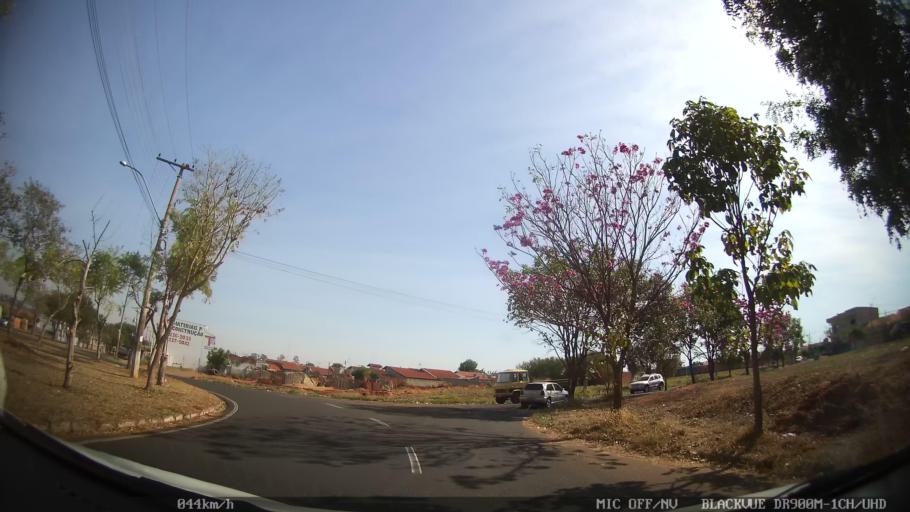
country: BR
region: Sao Paulo
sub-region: Sao Jose Do Rio Preto
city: Sao Jose do Rio Preto
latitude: -20.7903
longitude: -49.4385
